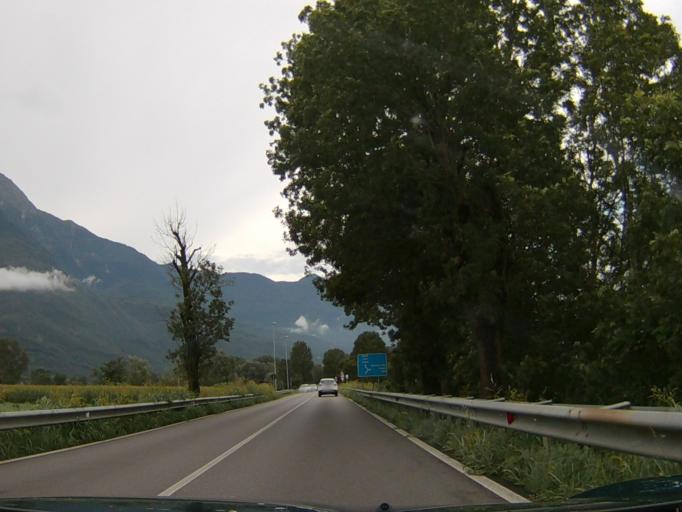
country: IT
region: Lombardy
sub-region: Provincia di Sondrio
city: Dubino
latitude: 46.1593
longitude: 9.4208
